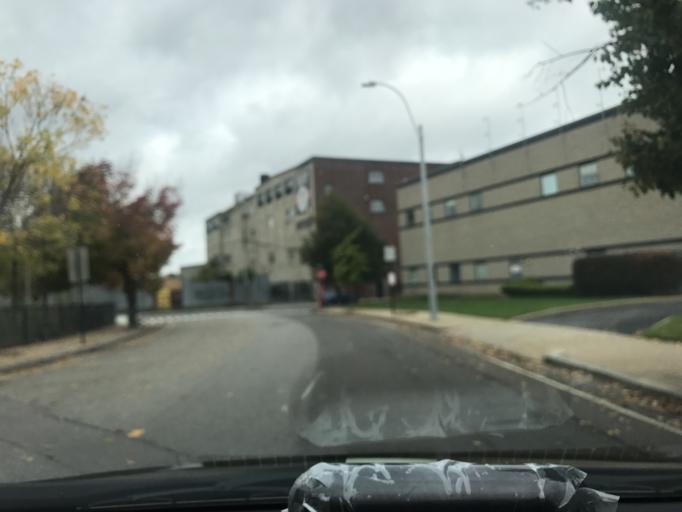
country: US
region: Massachusetts
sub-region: Middlesex County
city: Cambridge
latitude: 42.3751
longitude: -71.0921
